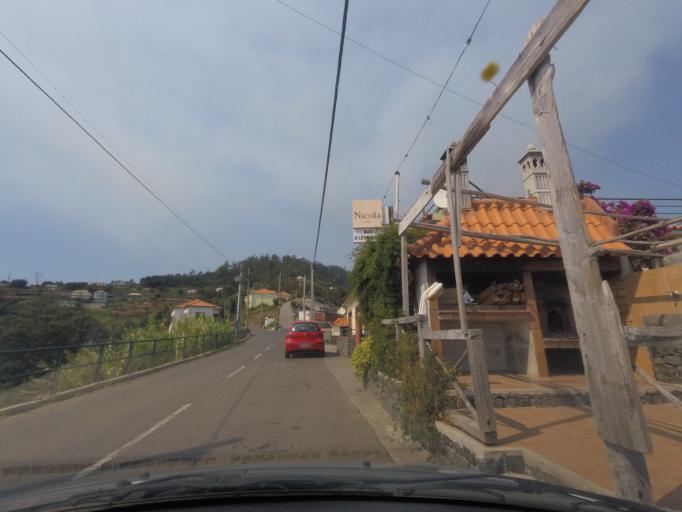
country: PT
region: Madeira
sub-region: Ribeira Brava
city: Campanario
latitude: 32.6918
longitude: -17.0569
